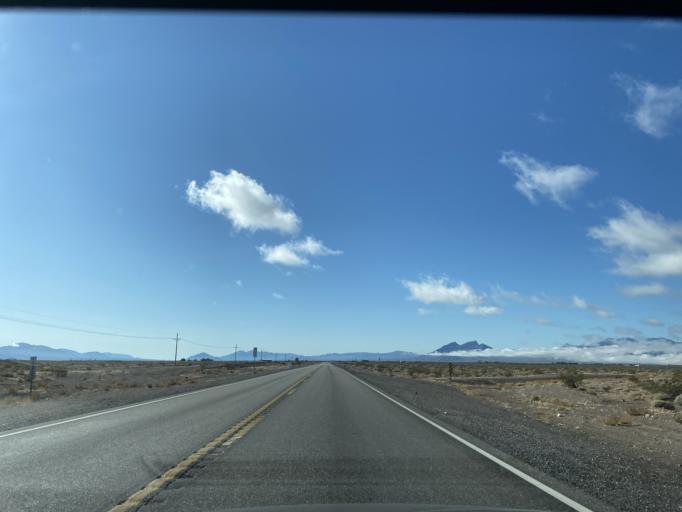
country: US
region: Nevada
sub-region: Nye County
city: Beatty
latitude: 36.5397
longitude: -116.4178
